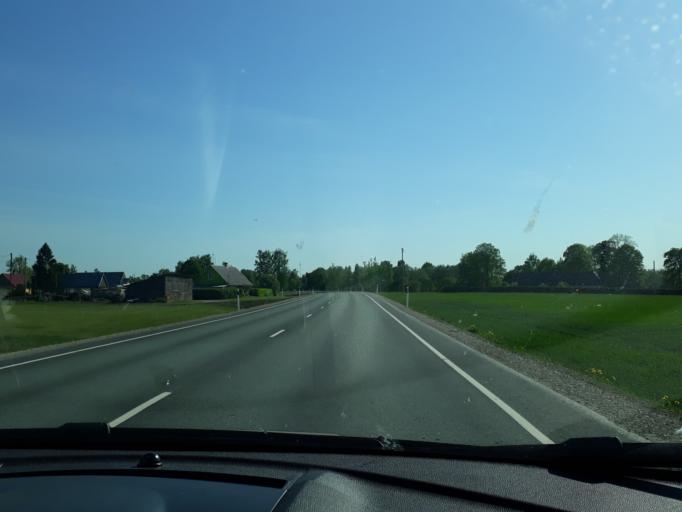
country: EE
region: Paernumaa
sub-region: Tootsi vald
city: Tootsi
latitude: 58.5386
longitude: 24.8377
